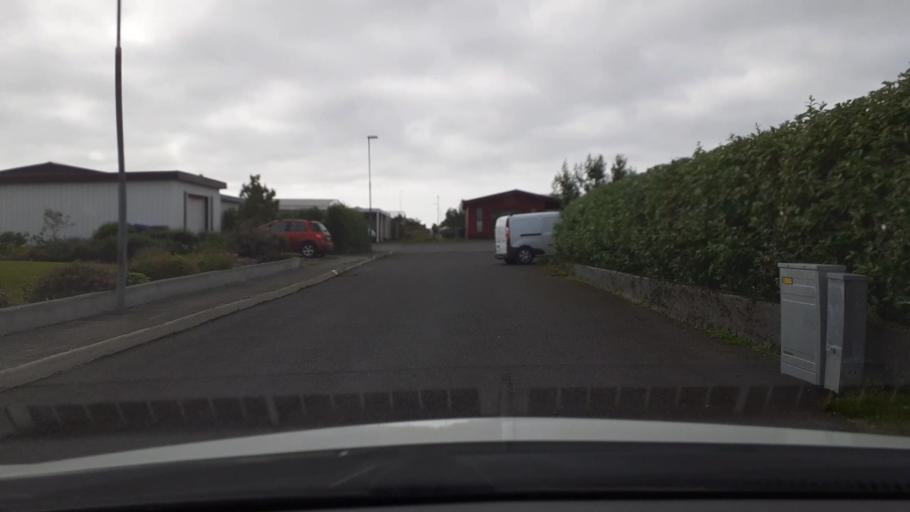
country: IS
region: South
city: THorlakshoefn
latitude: 63.8557
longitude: -21.3948
